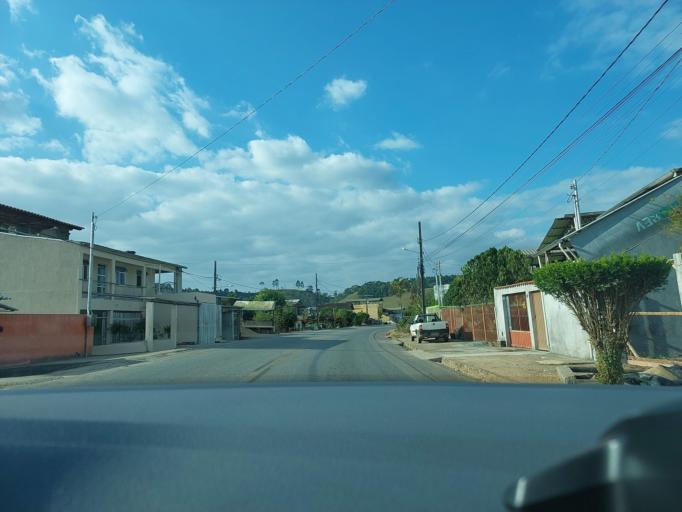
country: BR
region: Minas Gerais
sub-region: Vicosa
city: Vicosa
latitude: -20.8340
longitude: -42.7973
